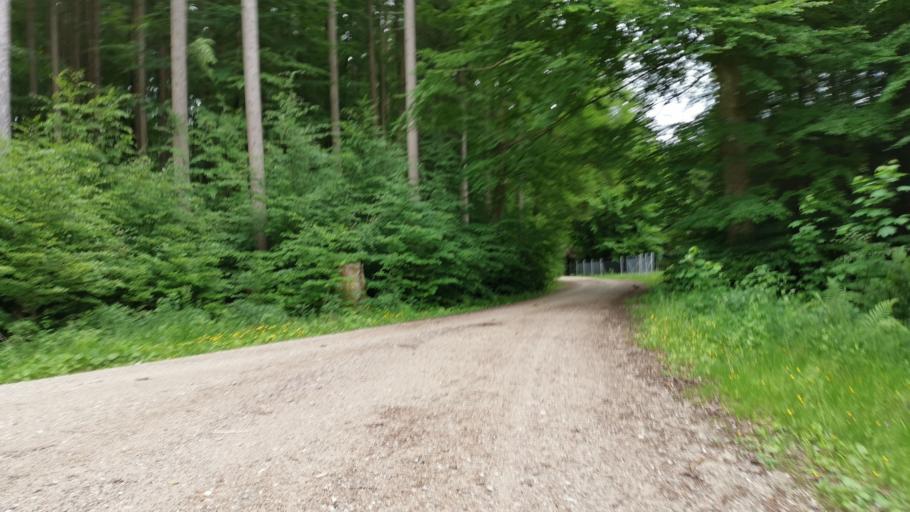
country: DE
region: Bavaria
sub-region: Upper Bavaria
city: Schaftlarn
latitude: 48.0066
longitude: 11.4400
